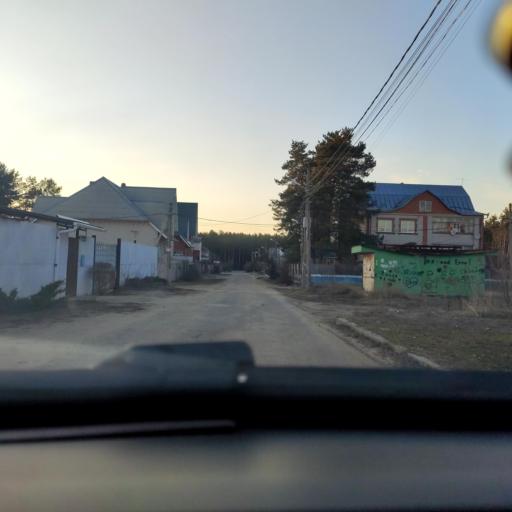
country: RU
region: Voronezj
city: Shilovo
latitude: 51.5776
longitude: 39.0443
